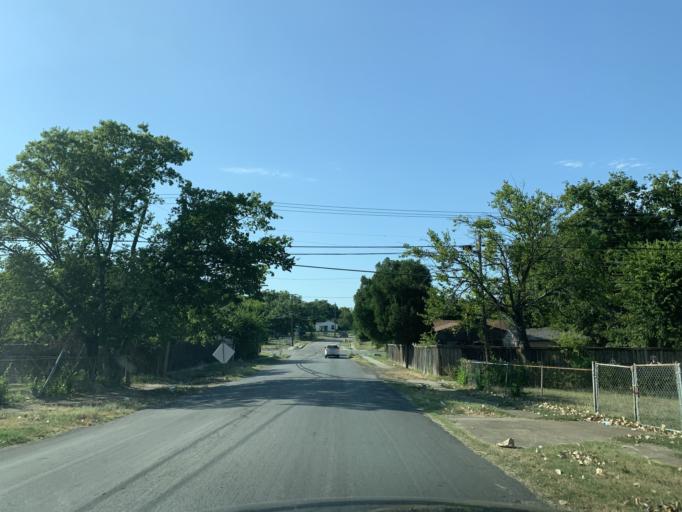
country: US
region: Texas
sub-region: Dallas County
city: Dallas
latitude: 32.7077
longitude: -96.7906
